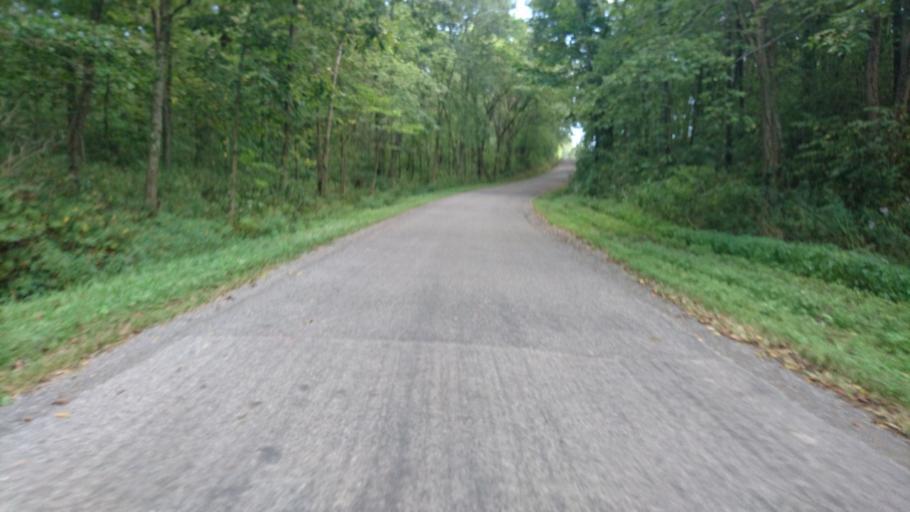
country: US
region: Illinois
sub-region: Macoupin County
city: Staunton
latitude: 38.9869
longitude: -89.7097
